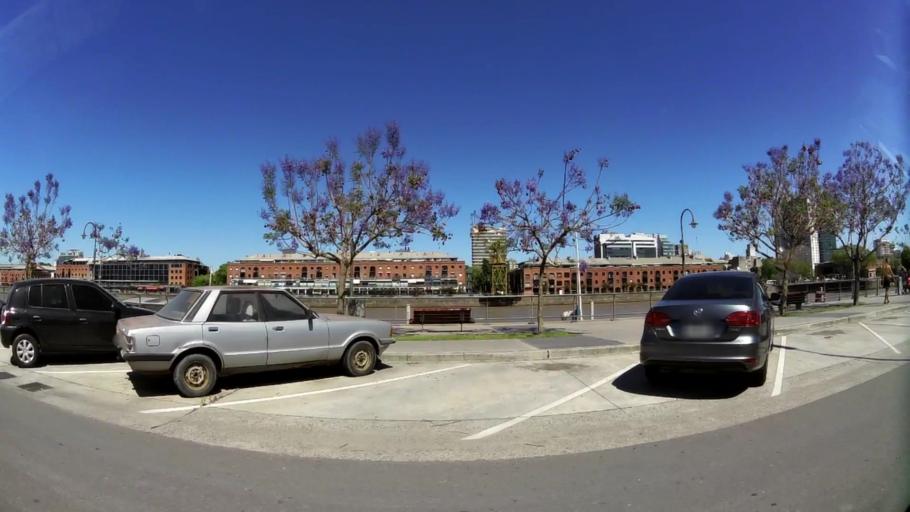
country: AR
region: Buenos Aires F.D.
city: Buenos Aires
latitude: -34.6197
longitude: -58.3626
